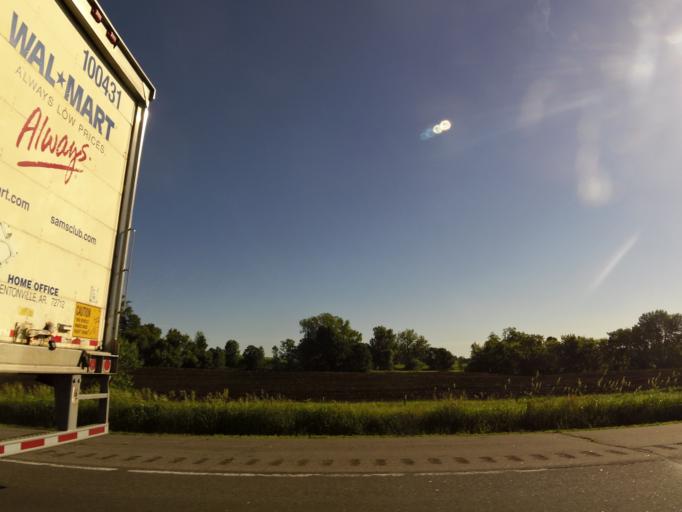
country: US
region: Minnesota
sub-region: Stearns County
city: Melrose
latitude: 45.6932
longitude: -94.8741
